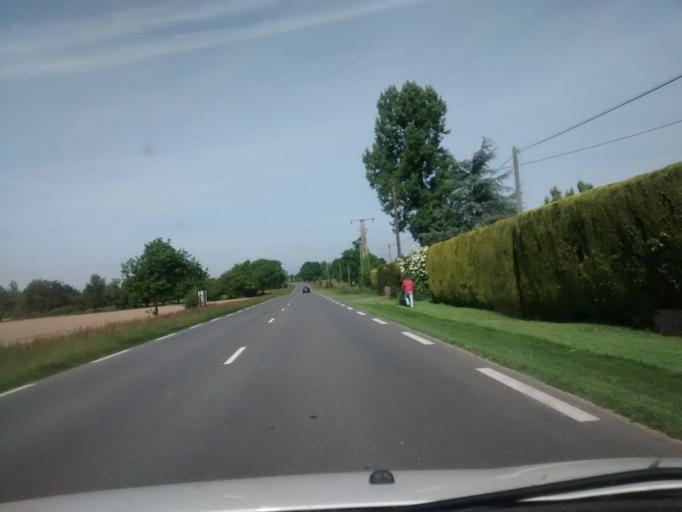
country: FR
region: Brittany
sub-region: Departement d'Ille-et-Vilaine
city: Saint-Brice-en-Cogles
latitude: 48.4191
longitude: -1.3967
